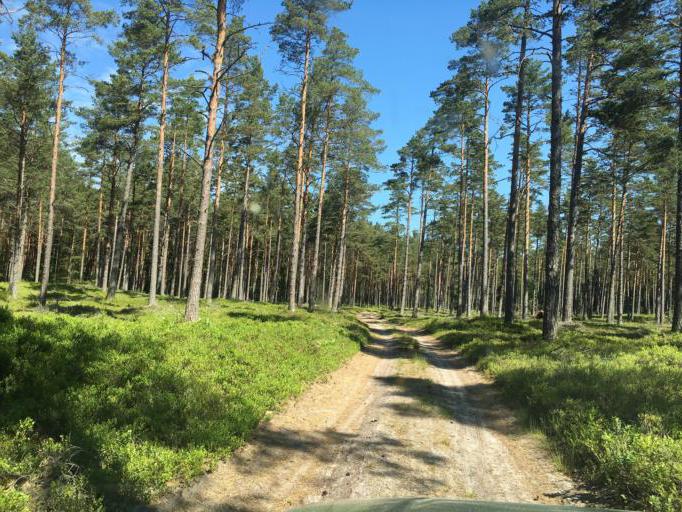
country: LV
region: Ventspils
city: Ventspils
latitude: 57.4766
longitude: 21.6485
